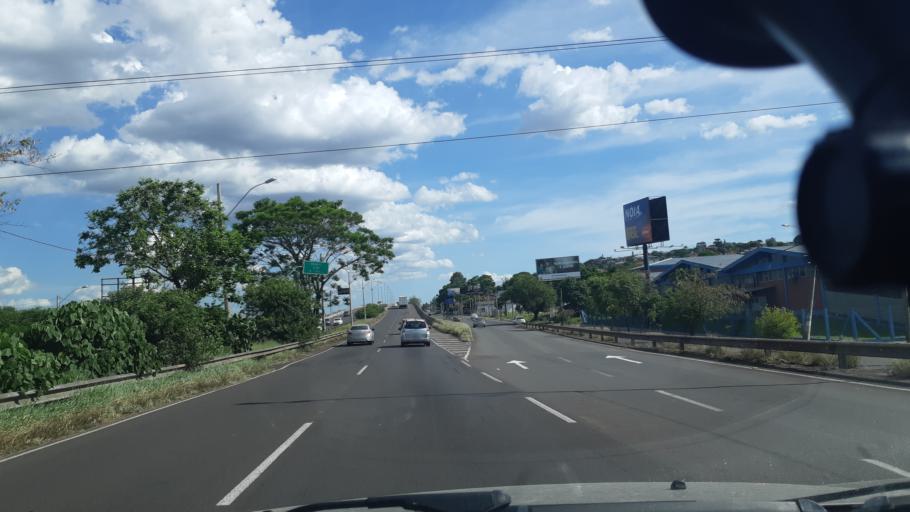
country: BR
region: Rio Grande do Sul
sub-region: Novo Hamburgo
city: Novo Hamburgo
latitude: -29.6658
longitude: -51.1435
